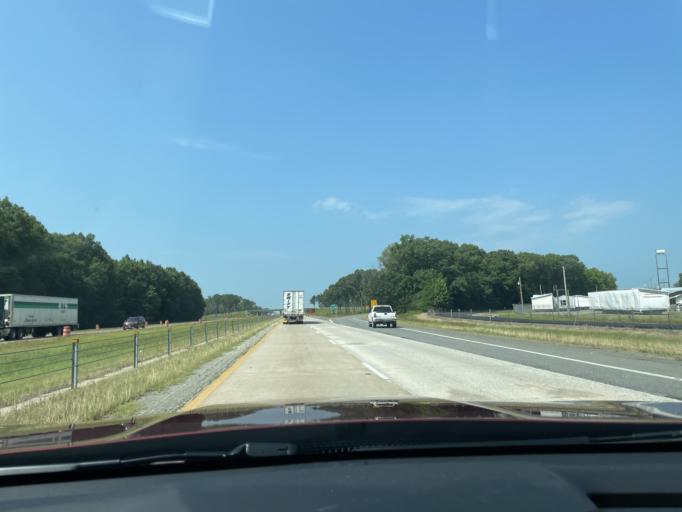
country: US
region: Arkansas
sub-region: White County
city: Searcy
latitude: 35.2078
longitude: -91.7281
